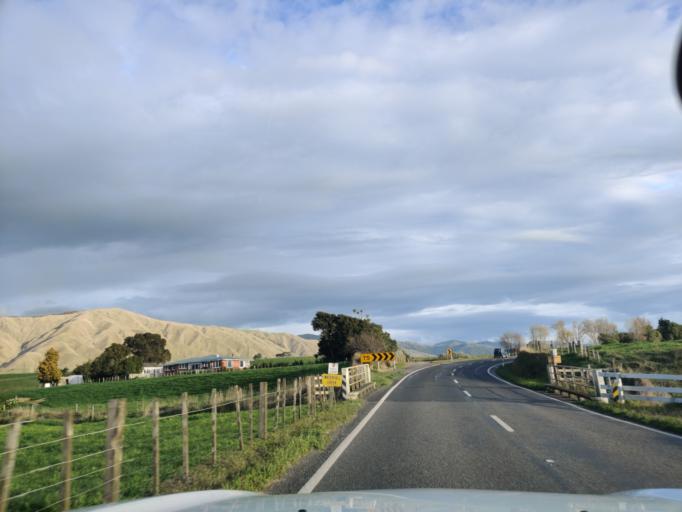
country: NZ
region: Manawatu-Wanganui
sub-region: Palmerston North City
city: Palmerston North
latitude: -40.4962
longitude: 175.4936
